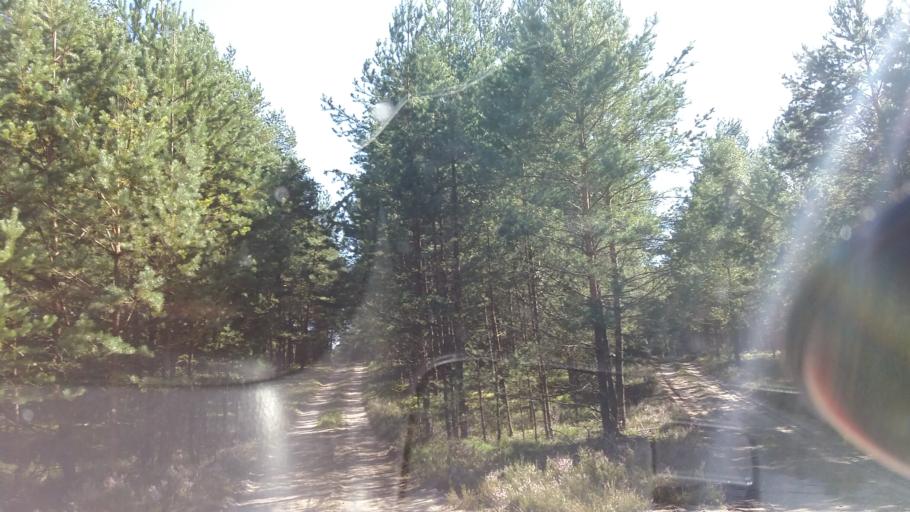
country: PL
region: West Pomeranian Voivodeship
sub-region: Powiat szczecinecki
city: Borne Sulinowo
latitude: 53.5836
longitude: 16.4967
